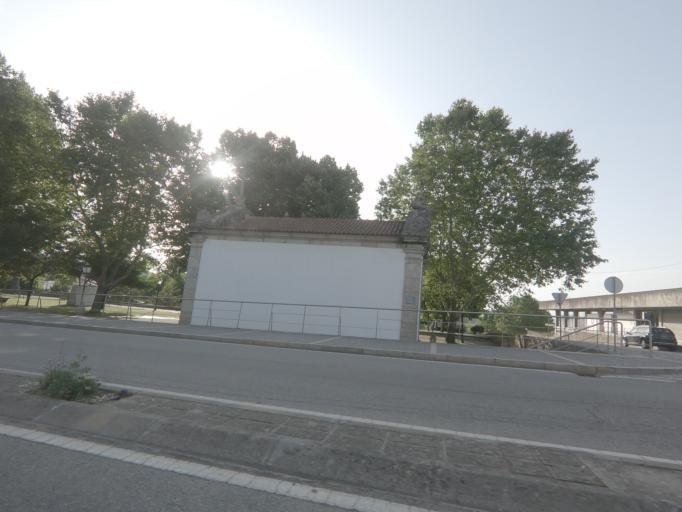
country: PT
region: Vila Real
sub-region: Sabrosa
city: Sabrosa
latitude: 41.2746
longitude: -7.4758
